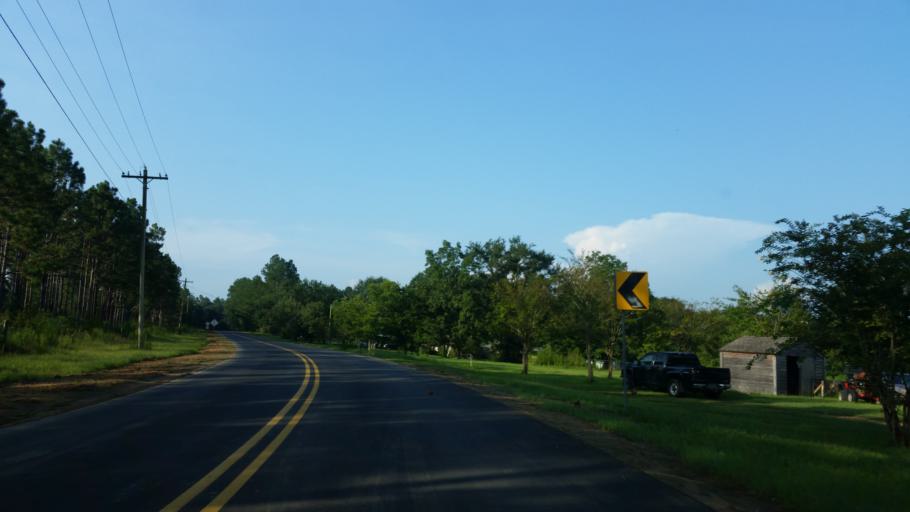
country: US
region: Alabama
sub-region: Baldwin County
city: Robertsdale
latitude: 30.5845
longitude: -87.5708
